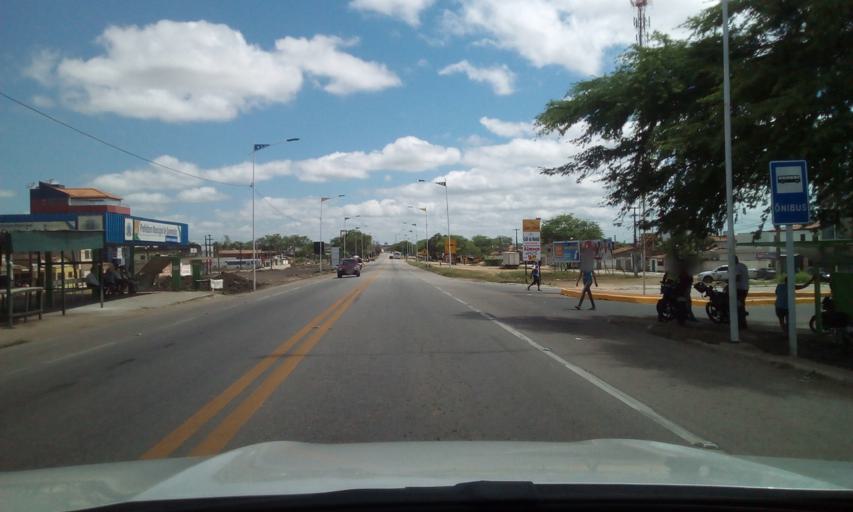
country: BR
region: Paraiba
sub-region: Campina Grande
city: Campina Grande
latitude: -7.2929
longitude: -35.8908
